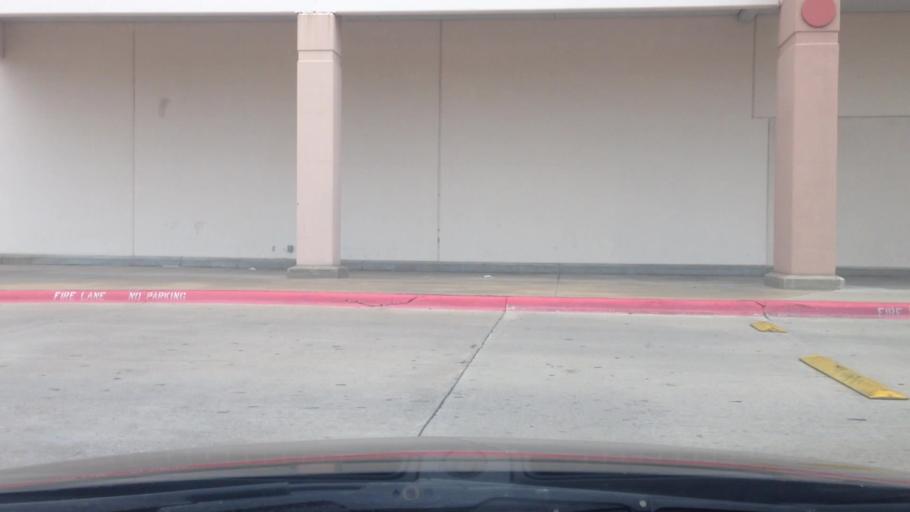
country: US
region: Texas
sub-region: Tarrant County
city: North Richland Hills
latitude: 32.8416
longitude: -97.2422
